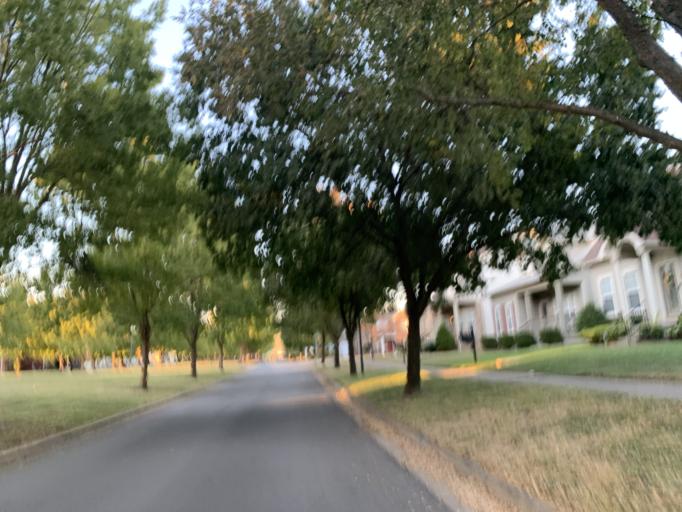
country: US
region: Kentucky
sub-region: Jefferson County
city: Shively
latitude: 38.2303
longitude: -85.8161
